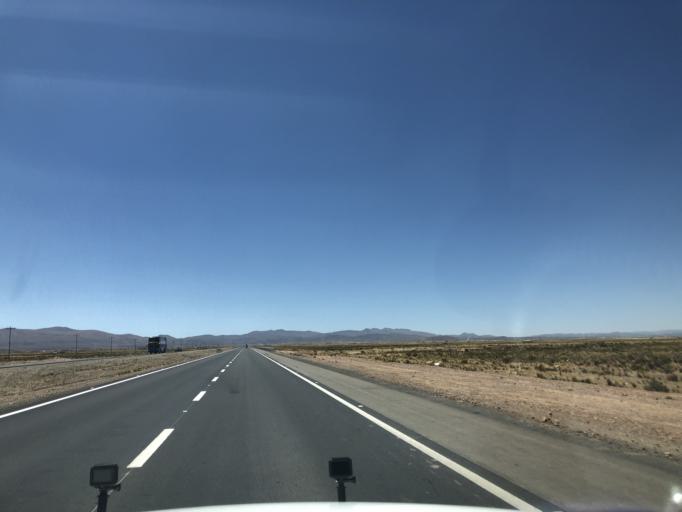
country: BO
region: La Paz
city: Colquiri
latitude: -17.6508
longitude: -67.1805
